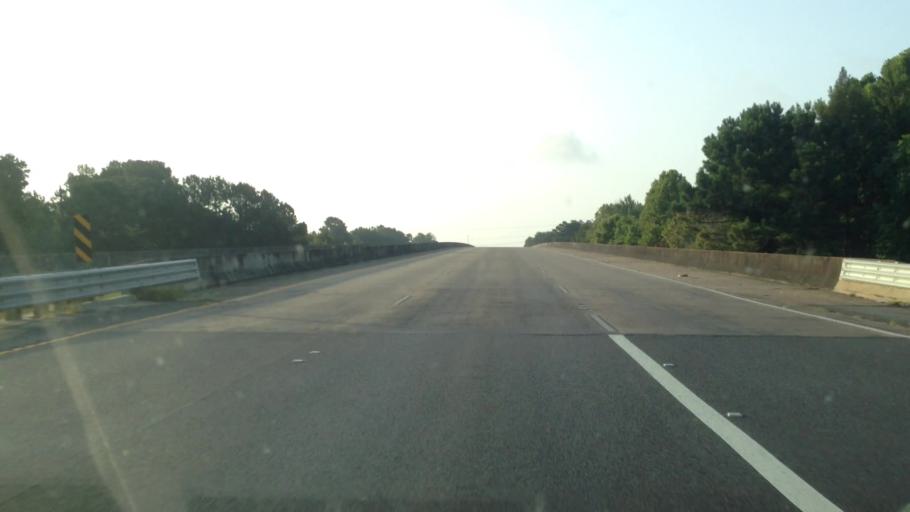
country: US
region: Louisiana
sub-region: Rapides Parish
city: Boyce
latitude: 31.4072
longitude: -92.7139
